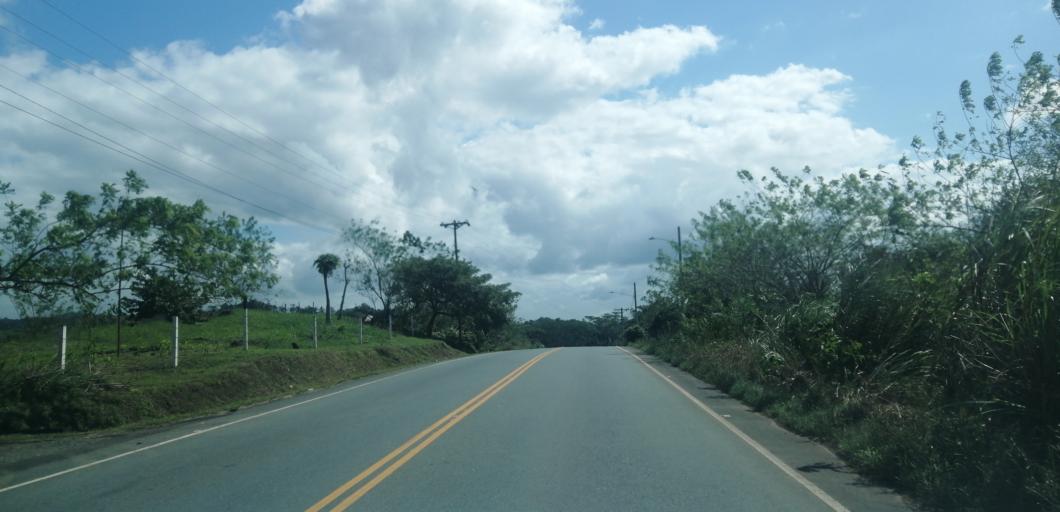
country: PA
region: Panama
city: Canita
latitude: 9.2214
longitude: -78.9212
